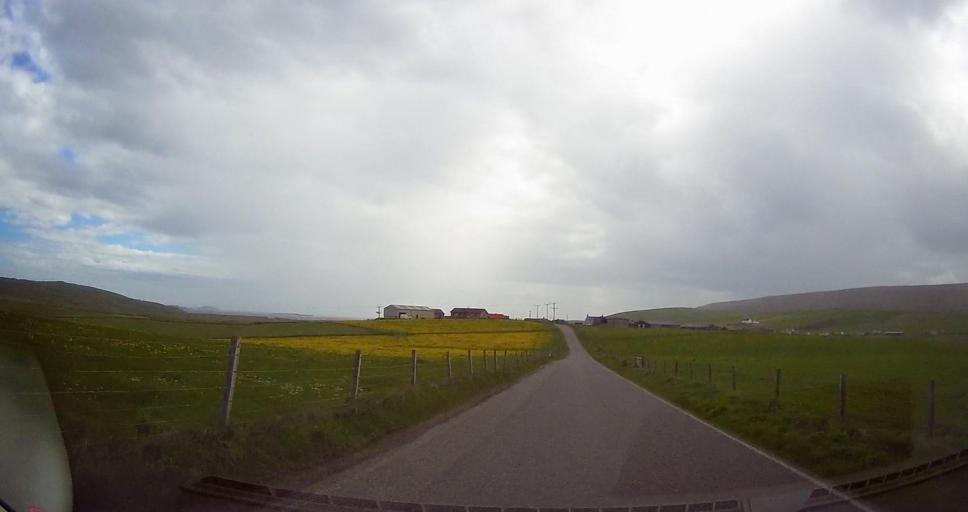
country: GB
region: Scotland
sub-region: Shetland Islands
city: Sandwick
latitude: 59.9157
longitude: -1.3214
